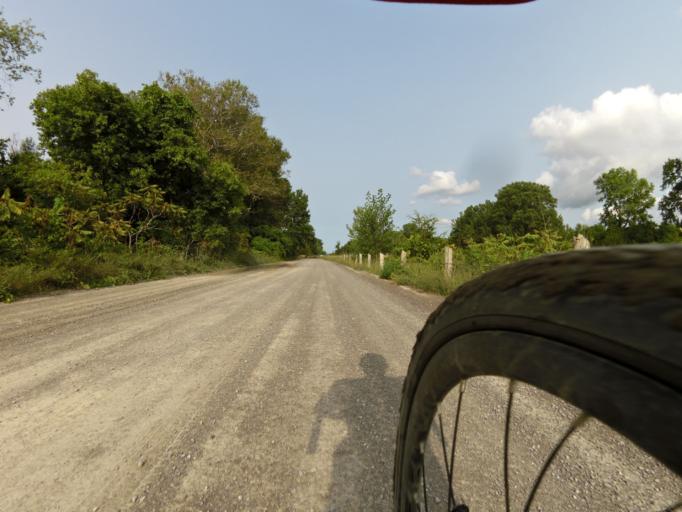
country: CA
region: Ontario
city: Quinte West
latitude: 44.0556
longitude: -77.6004
